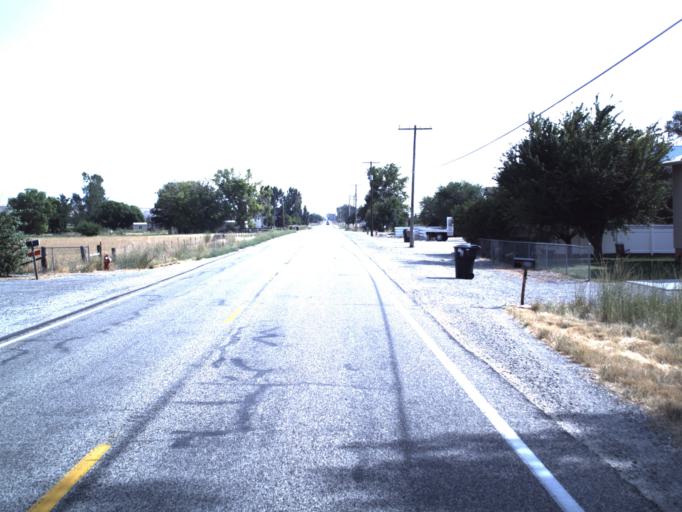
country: US
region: Utah
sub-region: Box Elder County
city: Elwood
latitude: 41.6919
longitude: -112.0900
